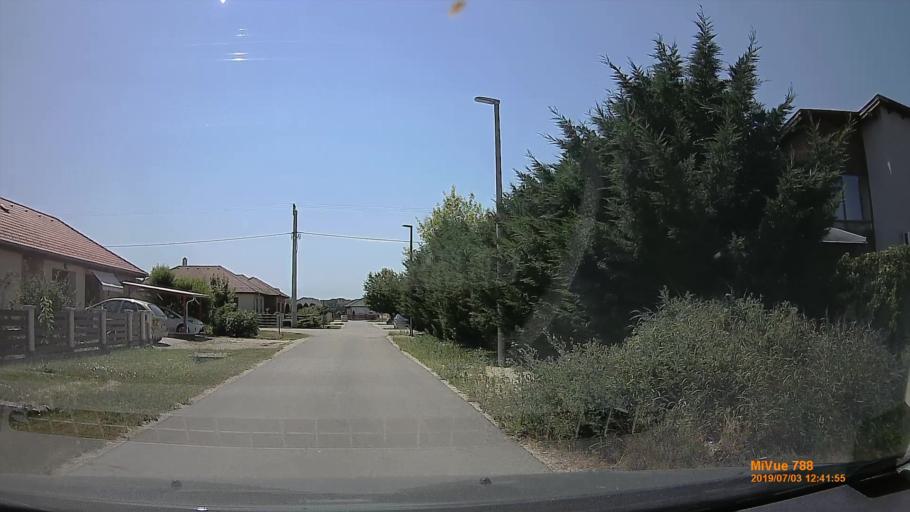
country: HU
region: Gyor-Moson-Sopron
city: Gyor
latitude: 47.7166
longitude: 17.6041
